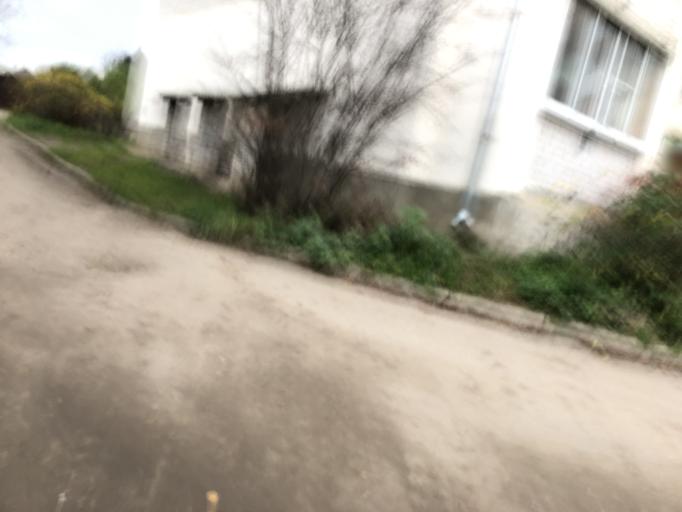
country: RU
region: Tverskaya
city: Rzhev
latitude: 56.2506
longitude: 34.3246
